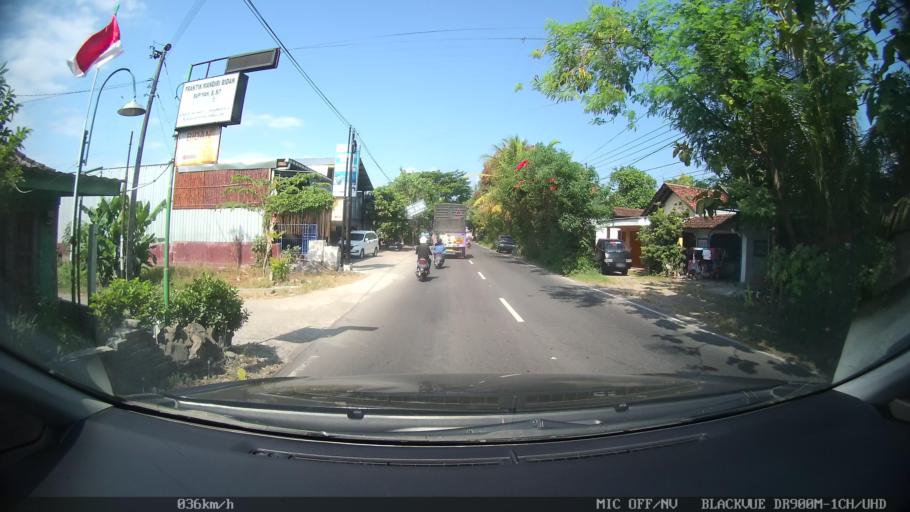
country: ID
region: Daerah Istimewa Yogyakarta
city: Sewon
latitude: -7.9127
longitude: 110.3689
